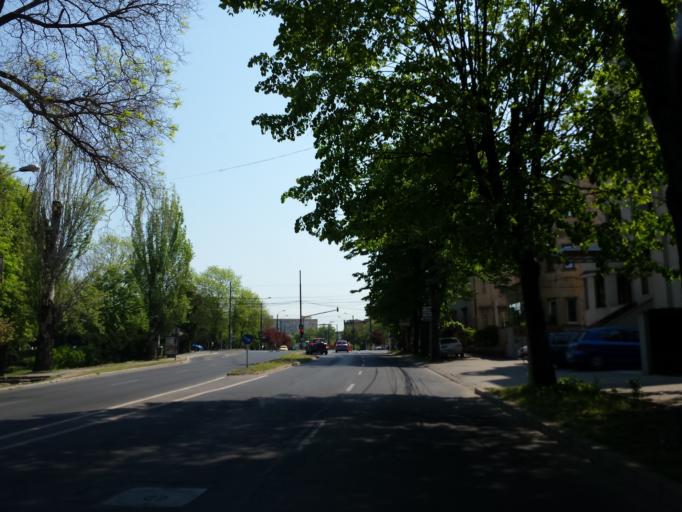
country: RO
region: Timis
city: Timisoara
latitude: 45.7481
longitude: 21.2241
